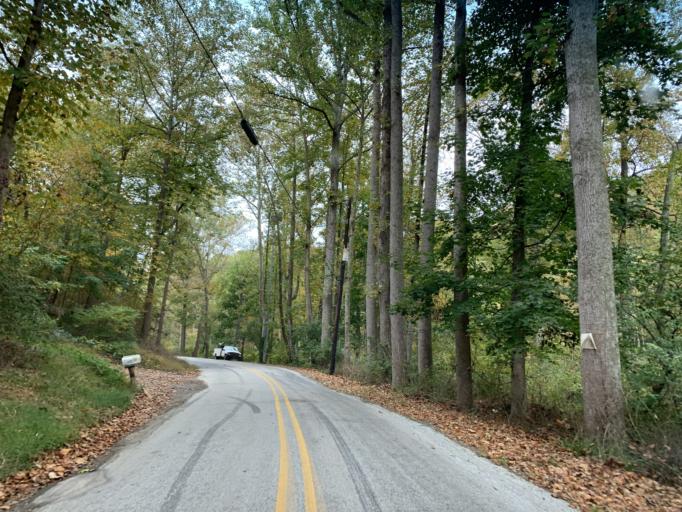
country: US
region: Pennsylvania
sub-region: York County
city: Susquehanna Trails
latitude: 39.7898
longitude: -76.4127
